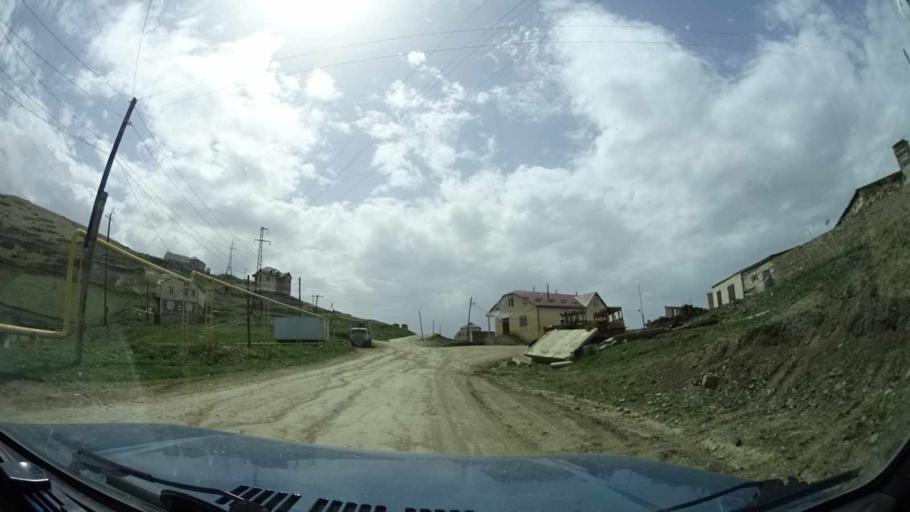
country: RU
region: Dagestan
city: Kubachi
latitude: 42.0916
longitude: 47.5899
